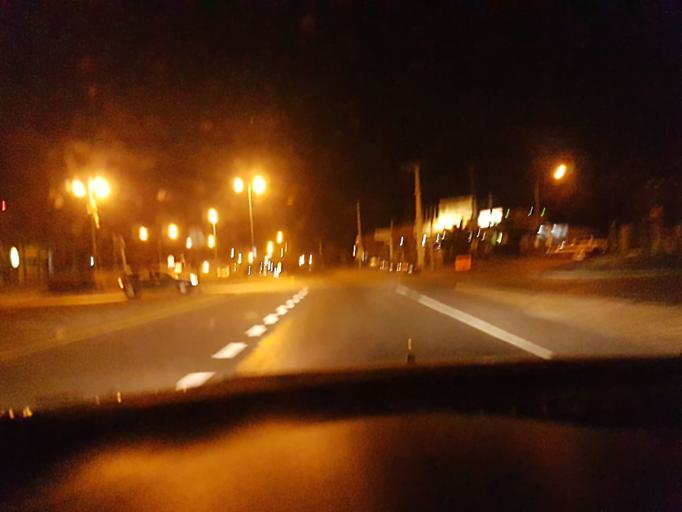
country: AR
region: Cordoba
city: Villa Allende
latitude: -31.3003
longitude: -64.2825
